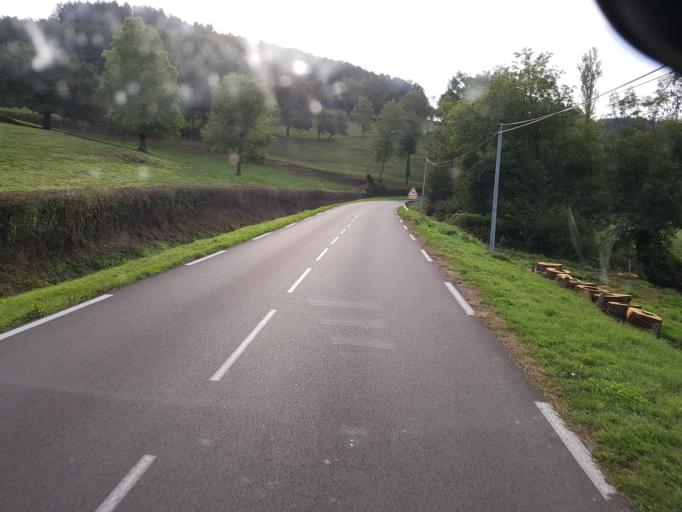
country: FR
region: Bourgogne
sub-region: Departement de Saone-et-Loire
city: La Clayette
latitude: 46.2785
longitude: 4.3734
